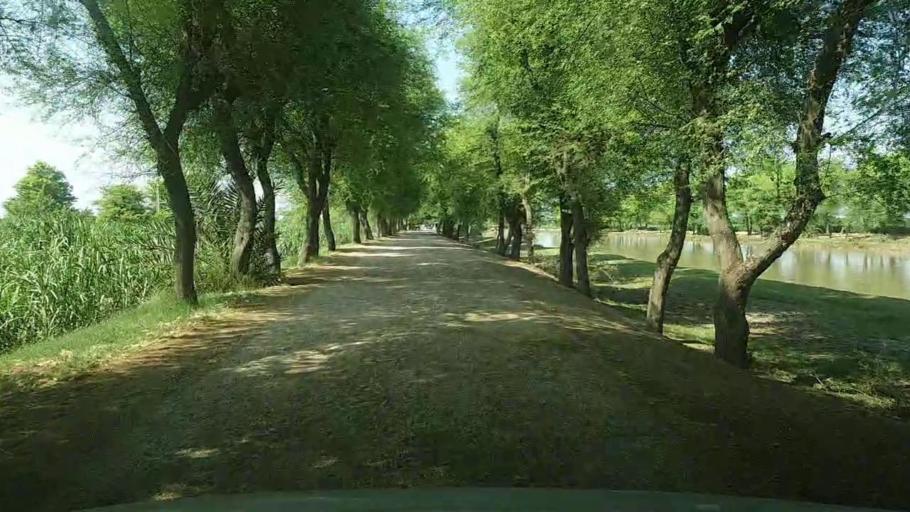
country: PK
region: Sindh
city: Mirpur Mathelo
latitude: 28.1197
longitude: 69.5974
